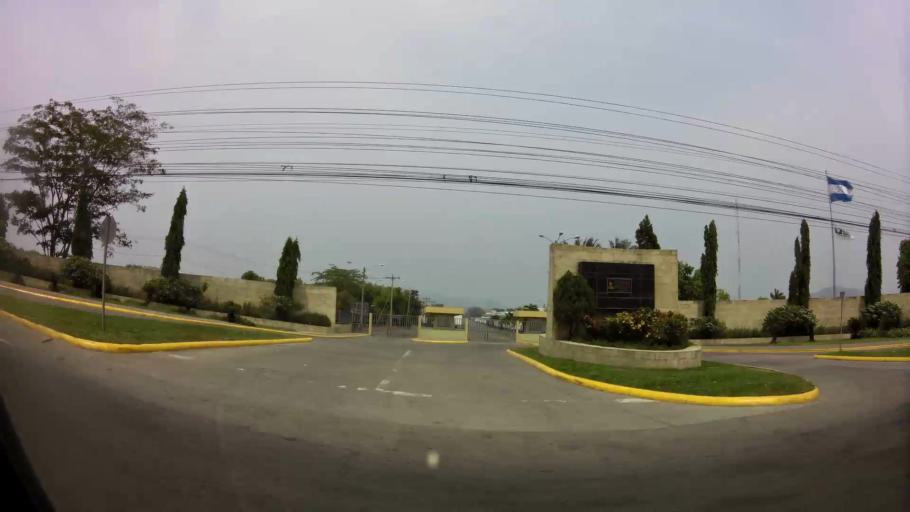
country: HN
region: Cortes
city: Villanueva
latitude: 15.3224
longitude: -87.9917
